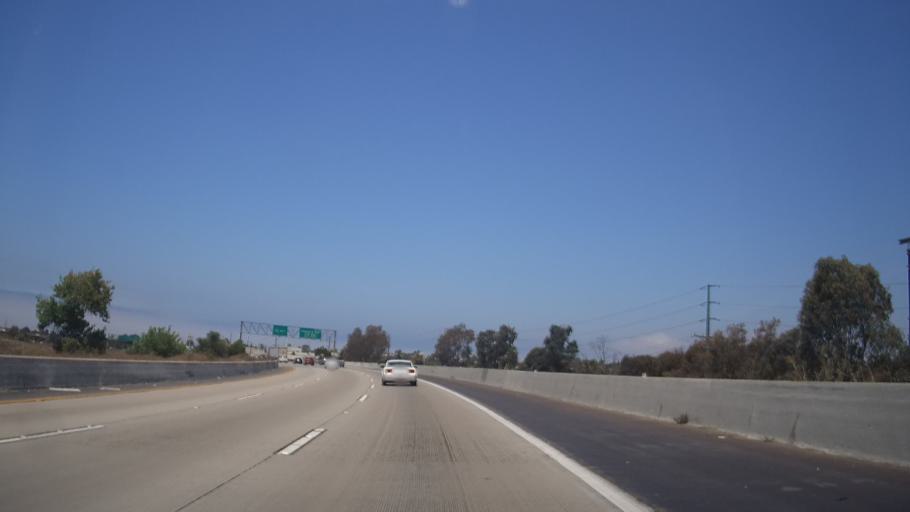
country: US
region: California
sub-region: San Diego County
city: Chula Vista
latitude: 32.6593
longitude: -117.0817
